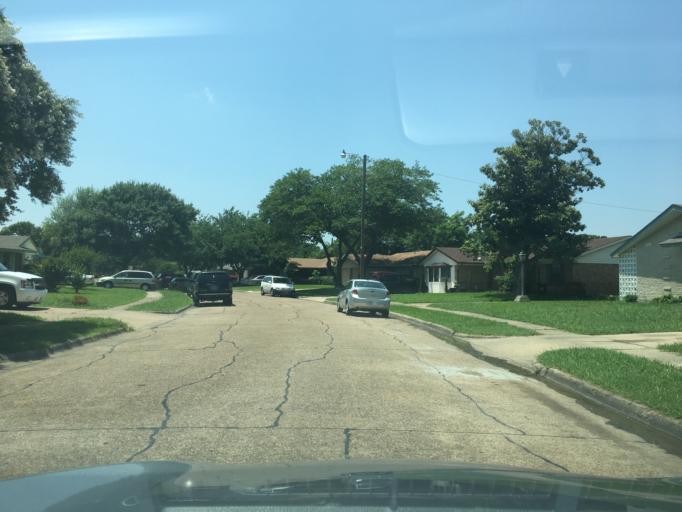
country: US
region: Texas
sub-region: Dallas County
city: Richardson
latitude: 32.9222
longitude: -96.7015
